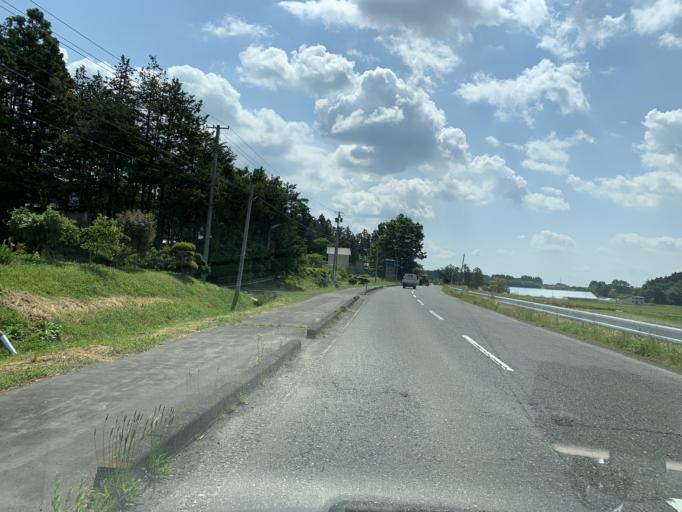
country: JP
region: Miyagi
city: Furukawa
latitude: 38.6878
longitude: 140.9506
